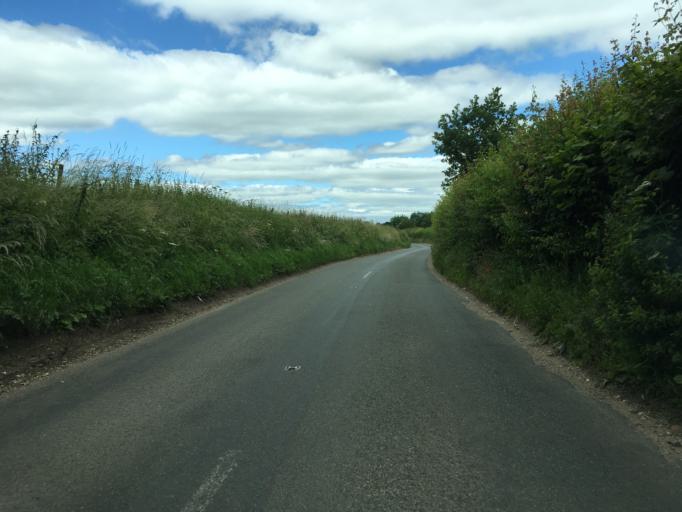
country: GB
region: England
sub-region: West Berkshire
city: Winterbourne
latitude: 51.4212
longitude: -1.3642
